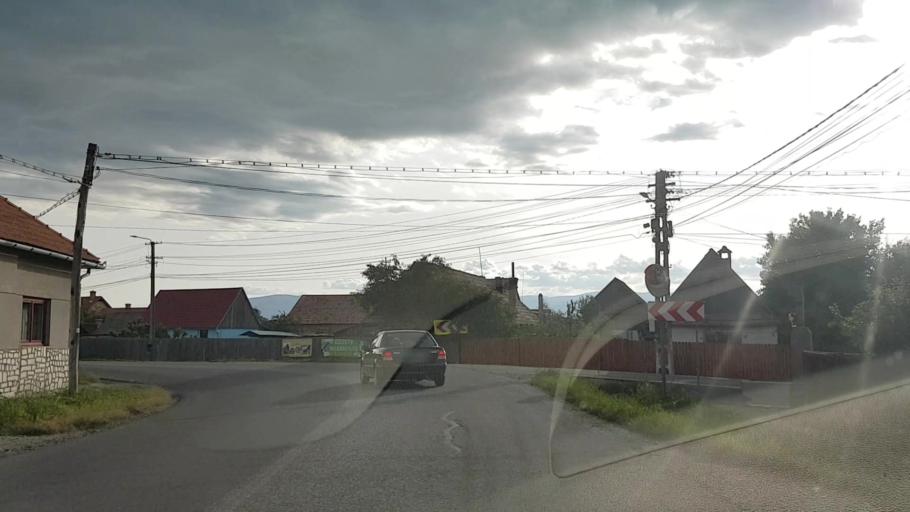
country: RO
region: Harghita
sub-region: Comuna Joseni
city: Joseni
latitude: 46.7034
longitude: 25.5153
